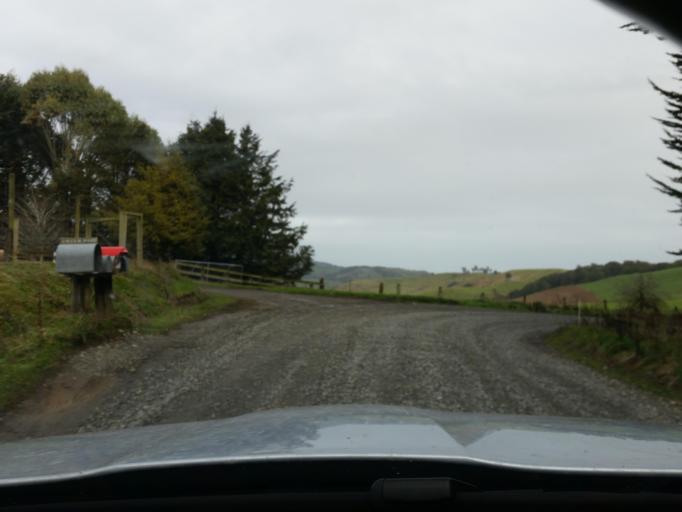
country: NZ
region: Southland
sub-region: Southland District
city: Riverton
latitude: -46.0676
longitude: 167.7703
